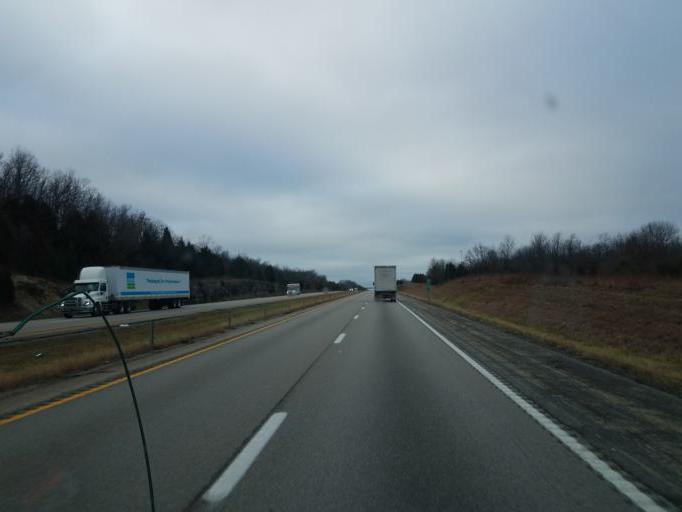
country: US
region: Missouri
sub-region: Laclede County
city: Lebanon
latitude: 37.5698
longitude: -92.7700
